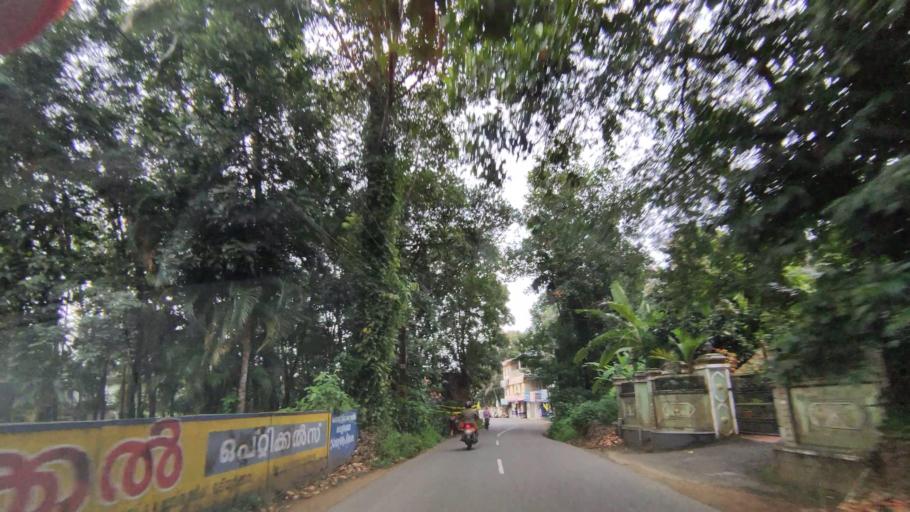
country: IN
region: Kerala
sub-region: Kottayam
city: Kottayam
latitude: 9.6779
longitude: 76.5058
